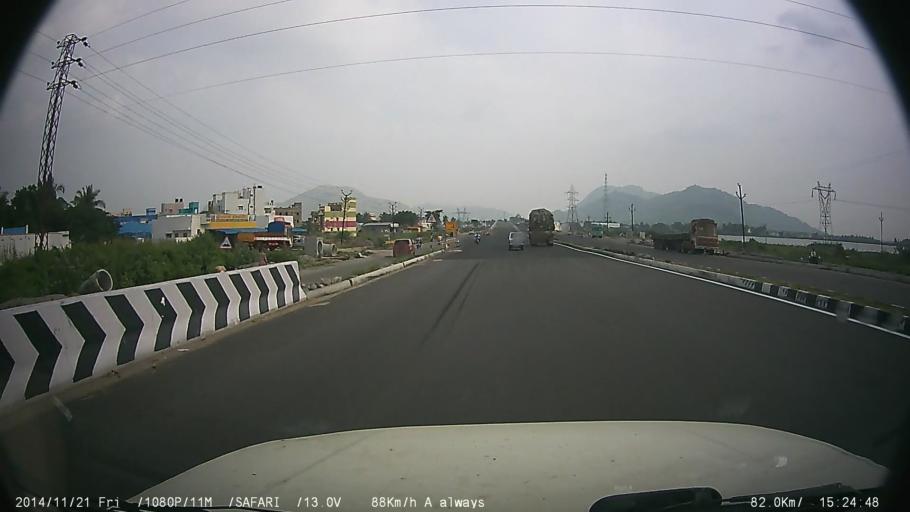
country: IN
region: Tamil Nadu
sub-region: Krishnagiri
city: Krishnagiri
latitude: 12.5124
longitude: 78.2194
